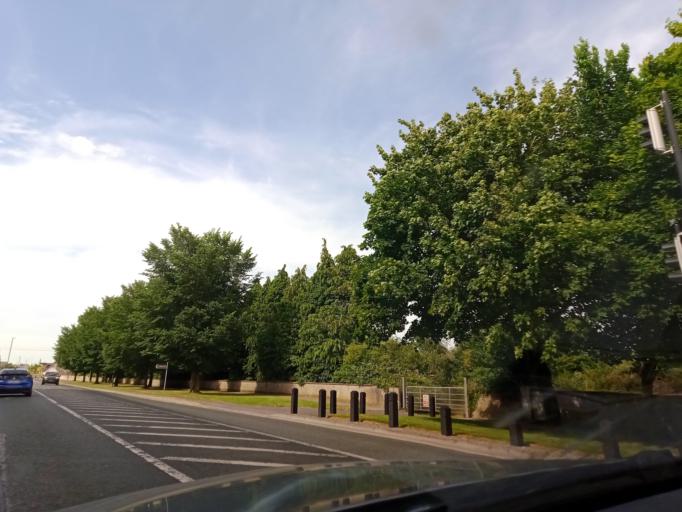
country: IE
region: Leinster
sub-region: Laois
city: Portlaoise
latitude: 53.0258
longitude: -7.2999
